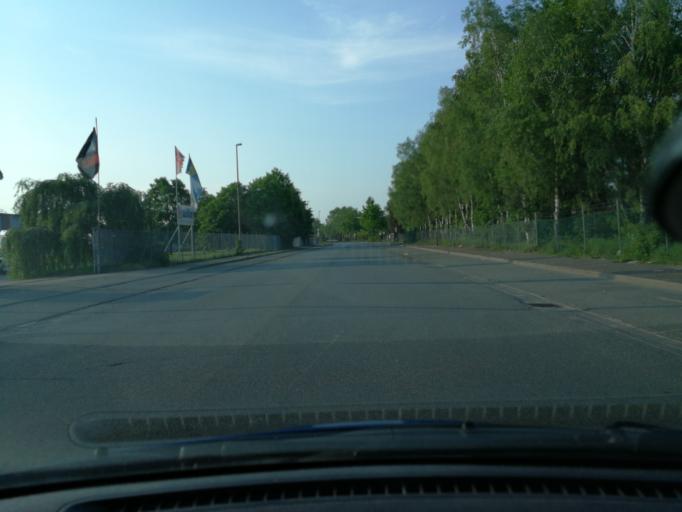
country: DE
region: Lower Saxony
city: Wendisch Evern
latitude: 53.2477
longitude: 10.4696
